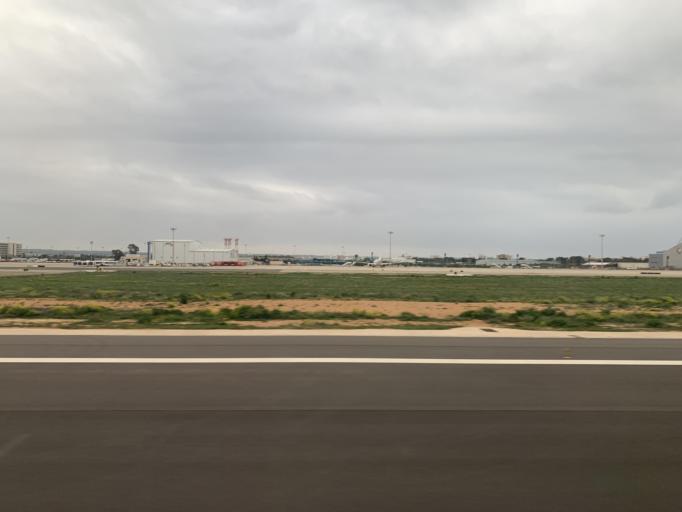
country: ES
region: Balearic Islands
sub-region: Illes Balears
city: s'Arenal
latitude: 39.5503
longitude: 2.7173
